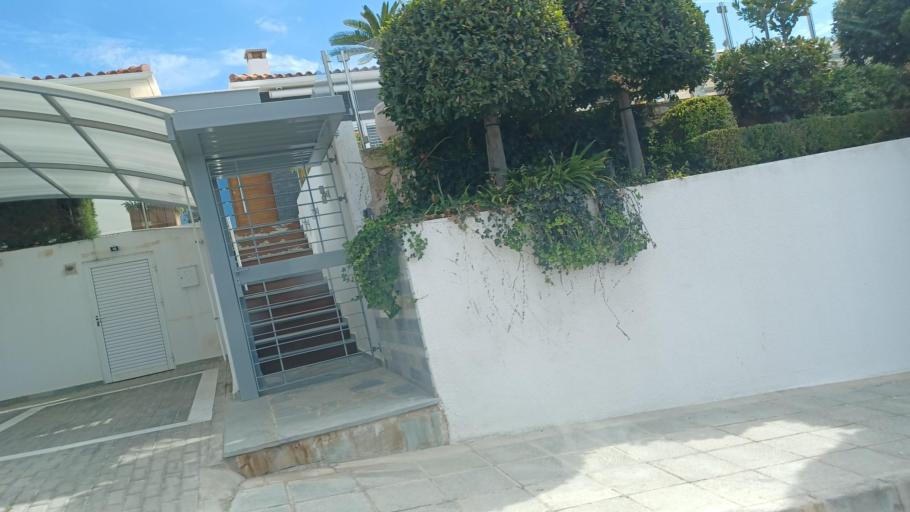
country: CY
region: Pafos
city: Mesogi
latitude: 34.8072
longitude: 32.4607
